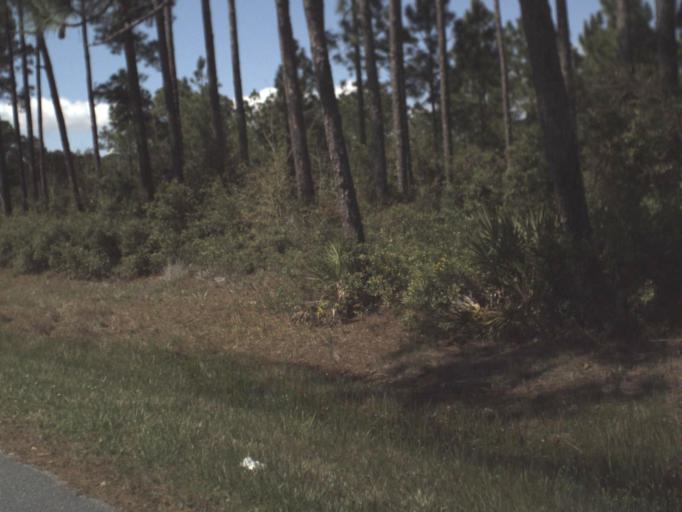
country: US
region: Florida
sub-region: Franklin County
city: Carrabelle
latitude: 29.9169
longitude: -84.5164
